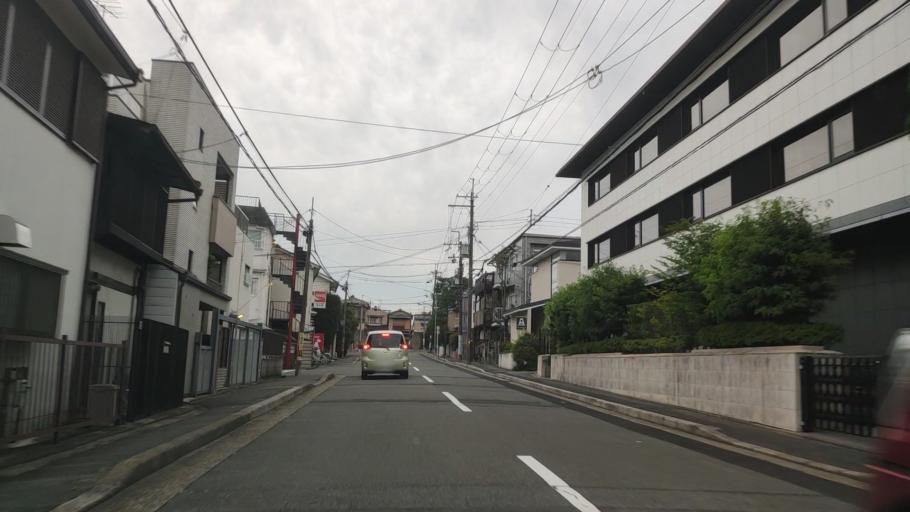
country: JP
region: Kyoto
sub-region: Kyoto-shi
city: Kamigyo-ku
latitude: 35.0247
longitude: 135.7885
